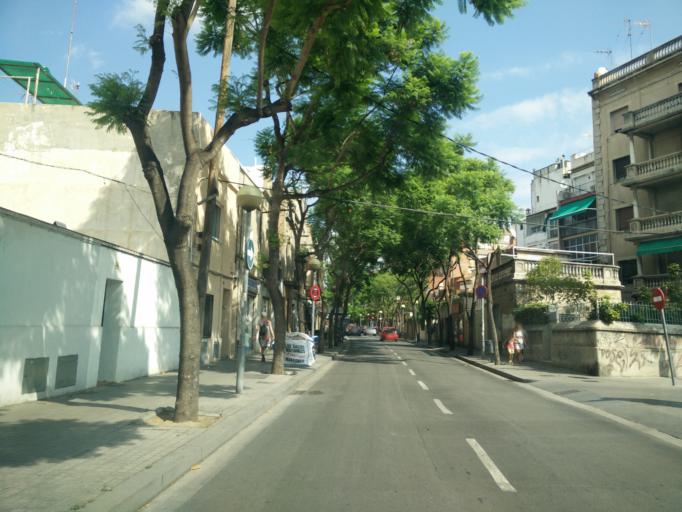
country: ES
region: Catalonia
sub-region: Provincia de Barcelona
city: Badalona
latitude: 41.4465
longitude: 2.2445
